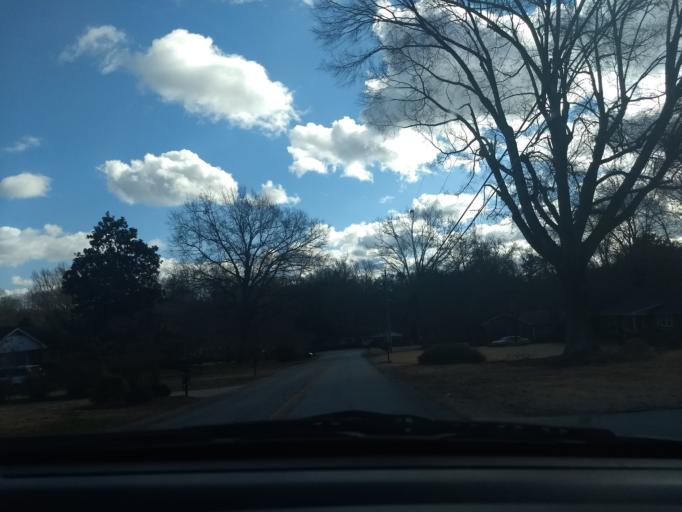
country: US
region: South Carolina
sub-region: Greenville County
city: Wade Hampton
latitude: 34.8768
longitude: -82.3548
